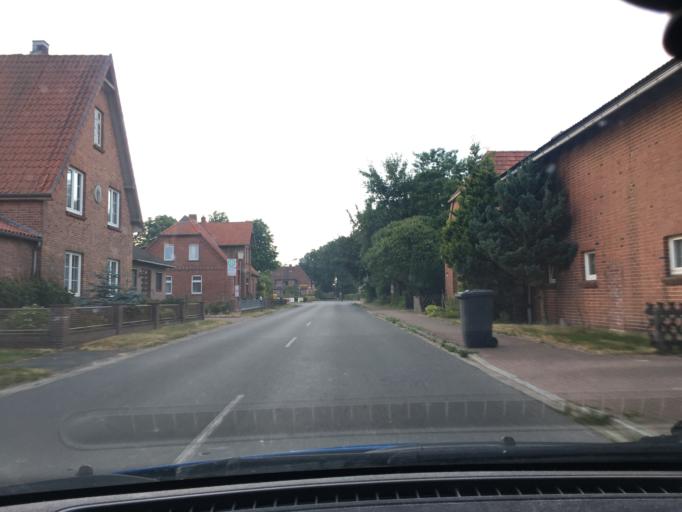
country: DE
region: Lower Saxony
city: Eyendorf
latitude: 53.1729
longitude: 10.1590
